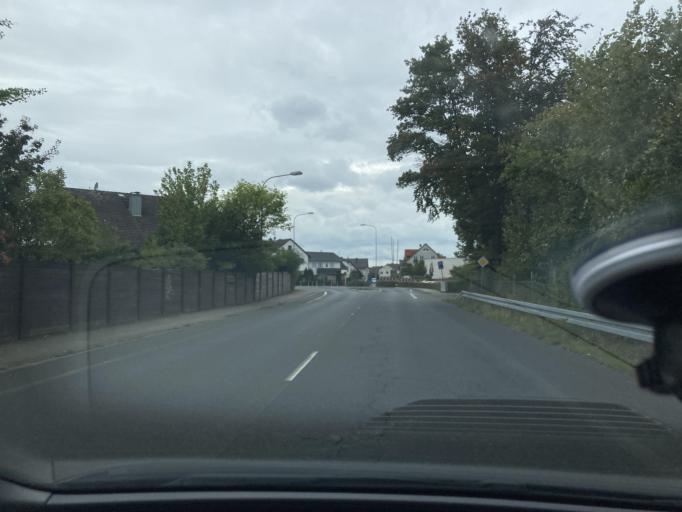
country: DE
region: Bavaria
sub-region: Regierungsbezirk Unterfranken
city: Kahl am Main
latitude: 50.0408
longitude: 9.0125
